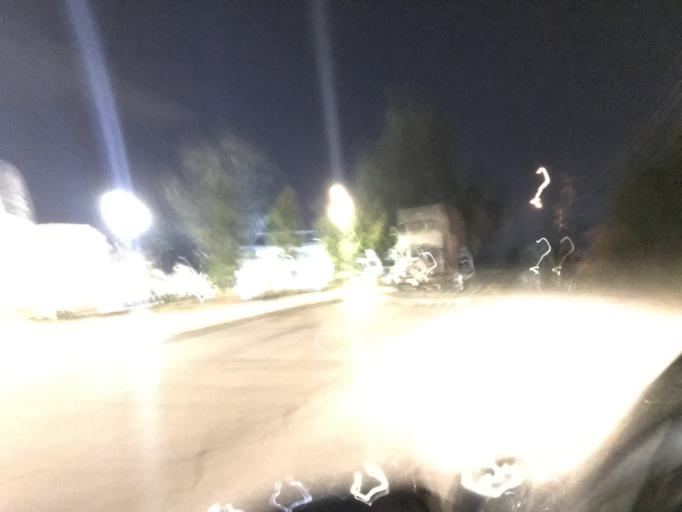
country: US
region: California
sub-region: San Diego County
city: La Mesa
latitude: 32.7815
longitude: -117.0347
